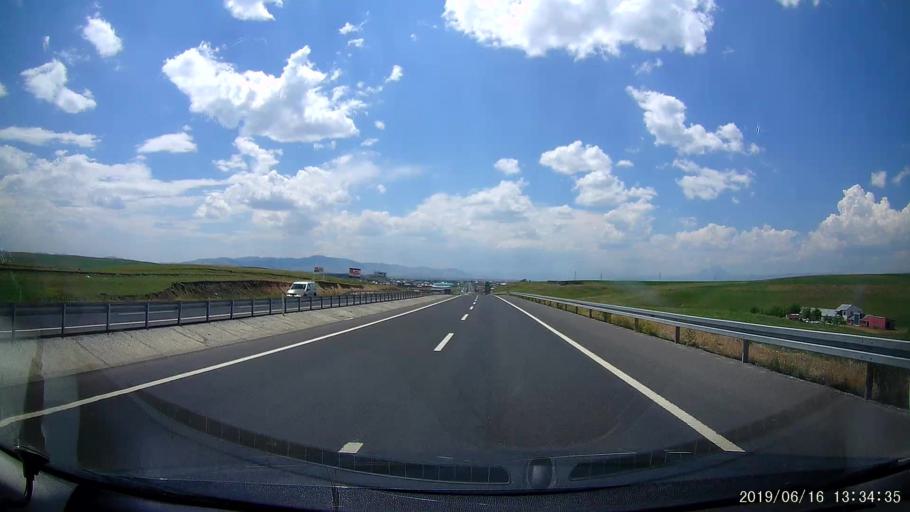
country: TR
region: Agri
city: Agri
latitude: 39.7130
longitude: 43.1222
